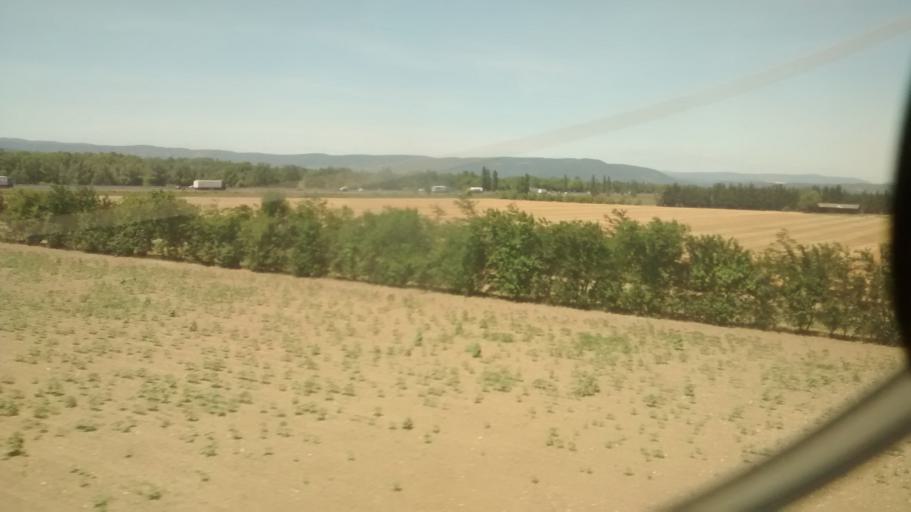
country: FR
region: Rhone-Alpes
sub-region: Departement de la Drome
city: La Garde-Adhemar
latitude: 44.3833
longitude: 4.7351
